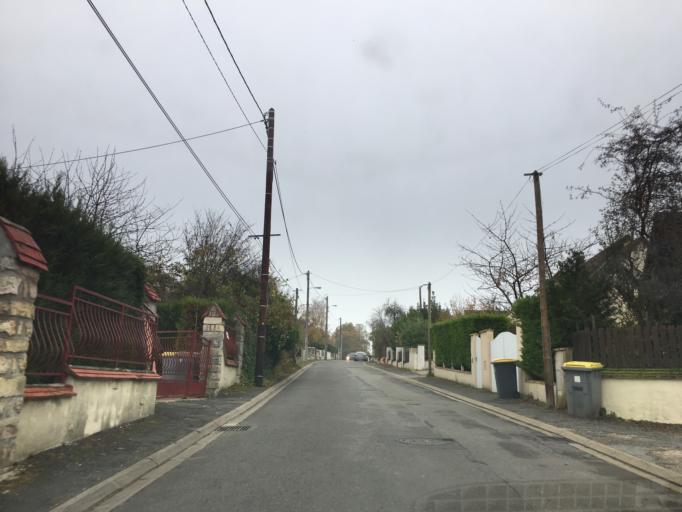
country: FR
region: Ile-de-France
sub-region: Departement de Seine-et-Marne
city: Moret-sur-Loing
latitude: 48.3684
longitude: 2.8094
